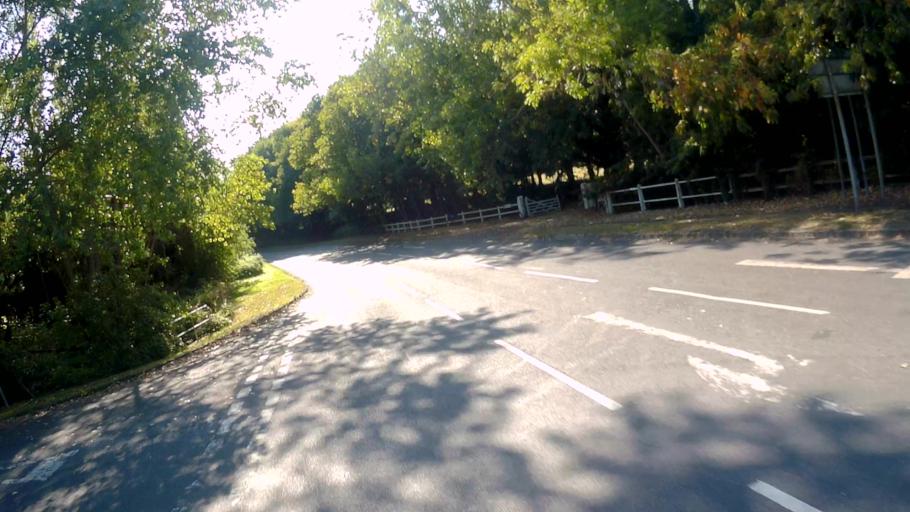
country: GB
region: England
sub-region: Hampshire
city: Long Sutton
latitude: 51.1864
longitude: -0.8935
